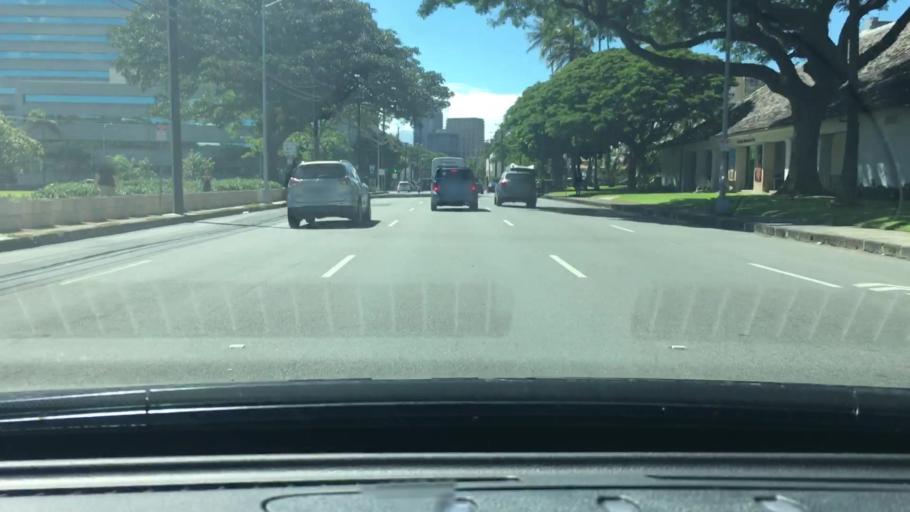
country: US
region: Hawaii
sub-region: Honolulu County
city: Honolulu
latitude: 21.3034
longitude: -157.8482
